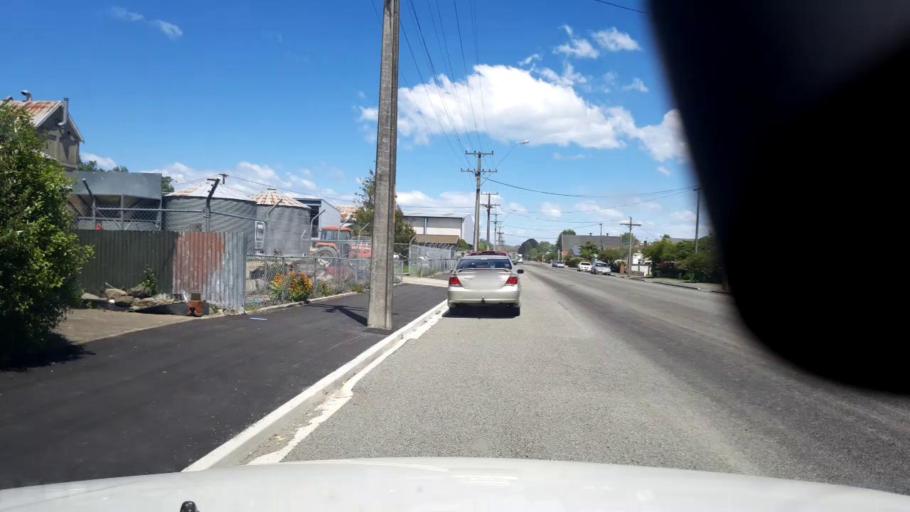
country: NZ
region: Canterbury
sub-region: Timaru District
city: Pleasant Point
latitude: -44.2379
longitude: 171.2794
